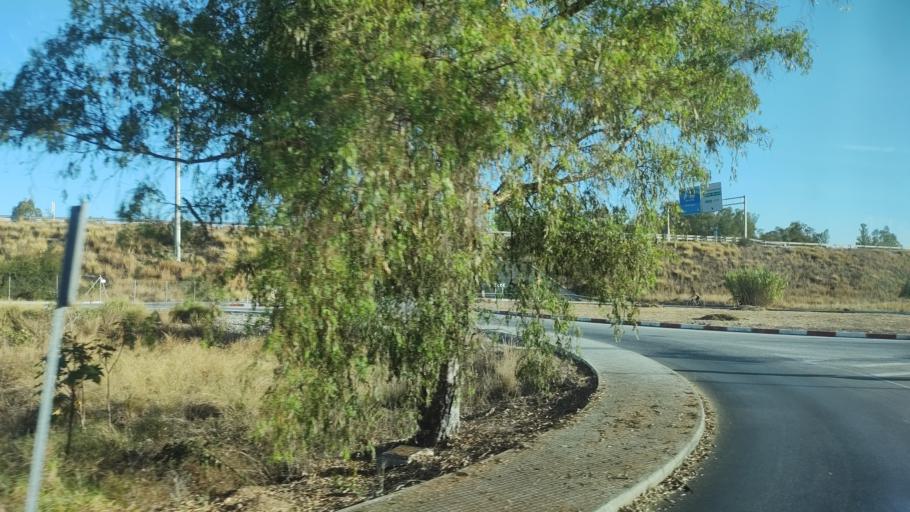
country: ES
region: Andalusia
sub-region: Provincia de Malaga
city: Torremolinos
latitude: 36.6486
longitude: -4.4820
